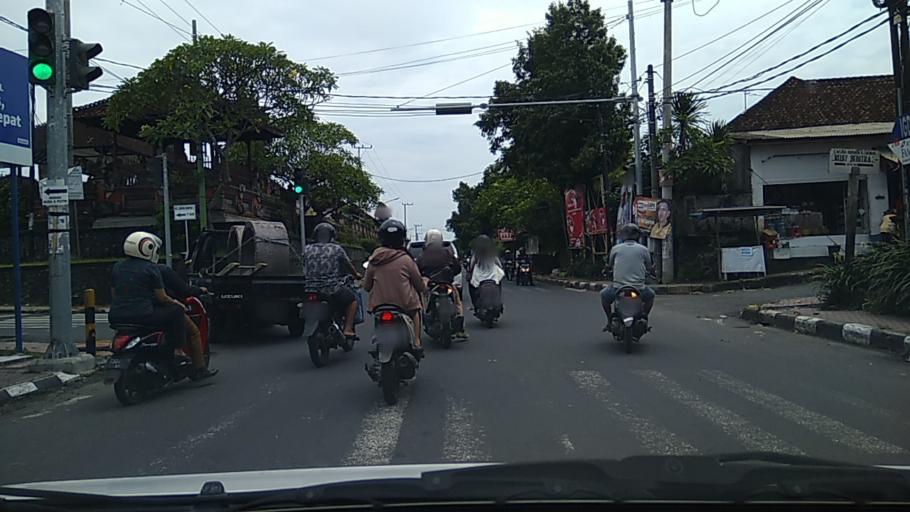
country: ID
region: Bali
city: Banjar Pesalakan
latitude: -8.5351
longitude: 115.3166
